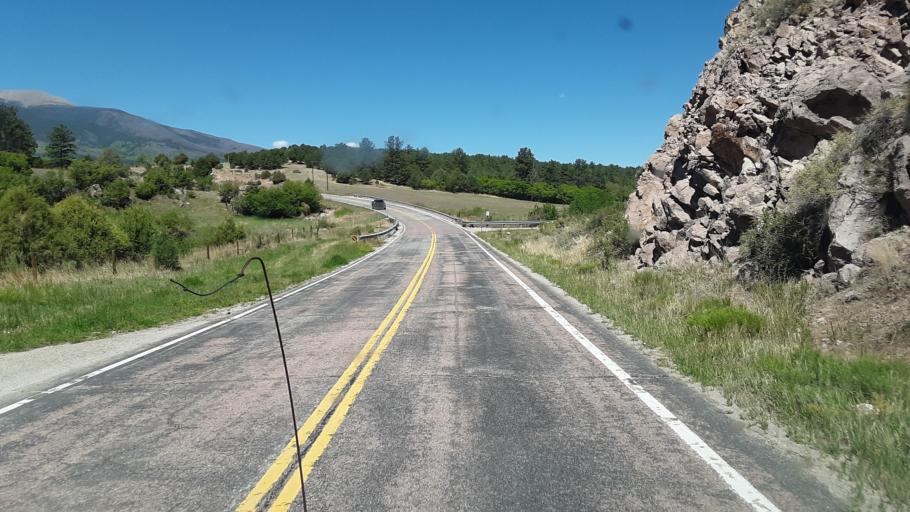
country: US
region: Colorado
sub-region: Custer County
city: Westcliffe
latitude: 38.2632
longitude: -105.6005
